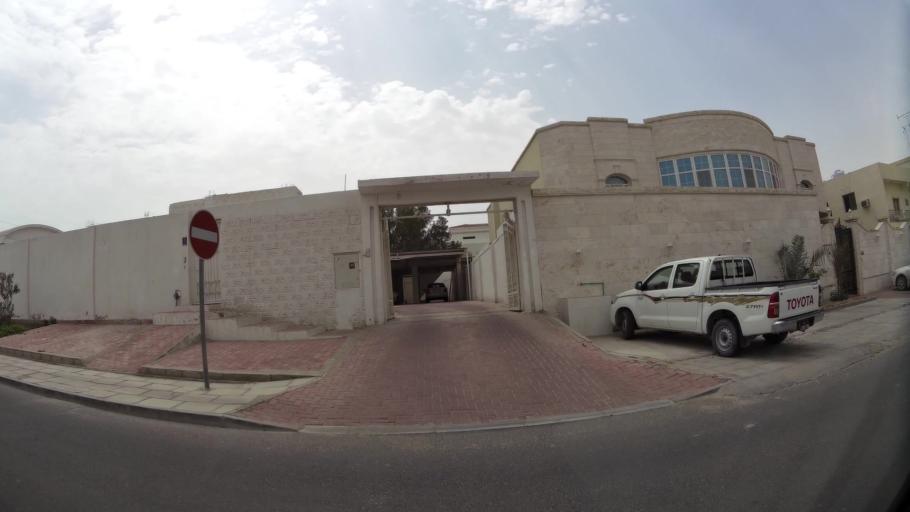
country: QA
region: Baladiyat ar Rayyan
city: Ar Rayyan
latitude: 25.3096
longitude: 51.4741
